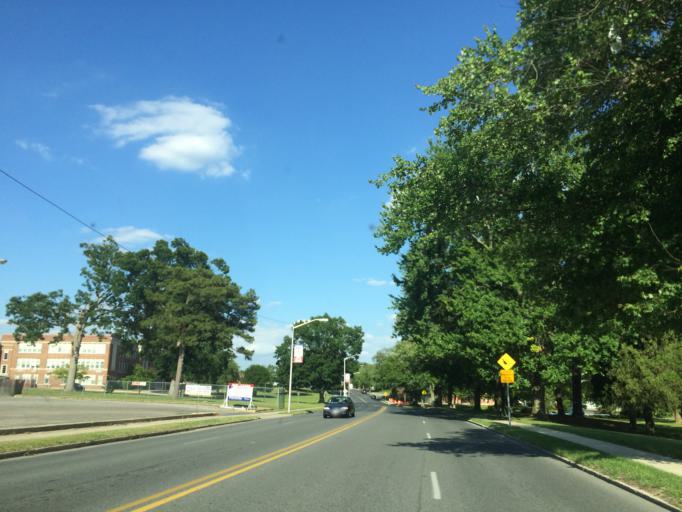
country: US
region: Maryland
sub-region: Wicomico County
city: Salisbury
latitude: 38.3653
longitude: -75.5913
